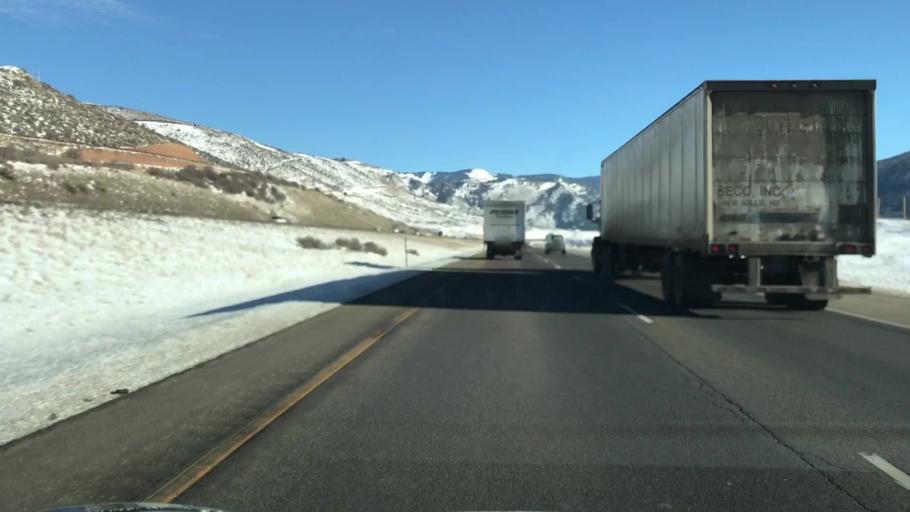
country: US
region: Colorado
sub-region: Eagle County
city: Avon
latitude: 39.6311
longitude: -106.5051
